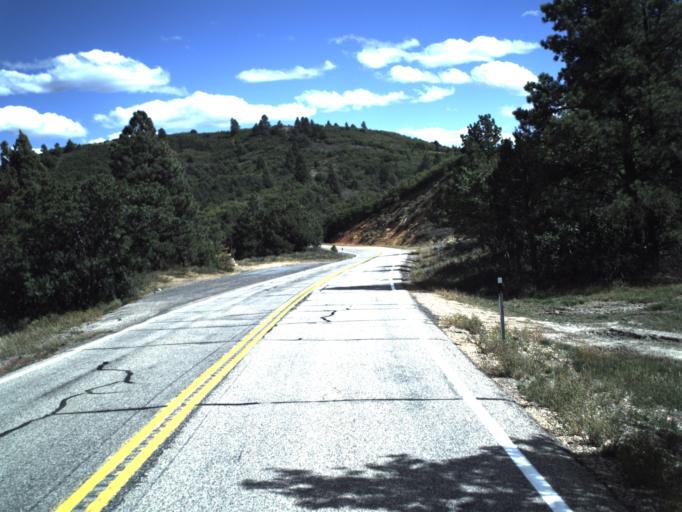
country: US
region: Utah
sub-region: Garfield County
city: Panguitch
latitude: 37.4966
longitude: -112.5435
